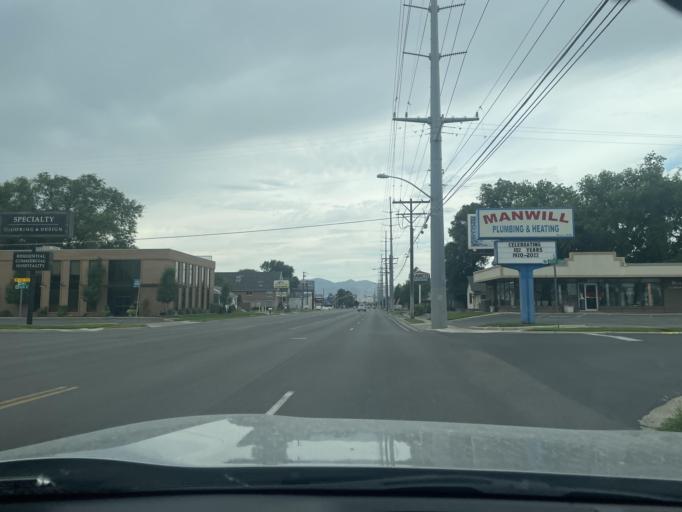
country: US
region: Utah
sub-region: Salt Lake County
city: Millcreek
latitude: 40.6871
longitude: -111.8797
